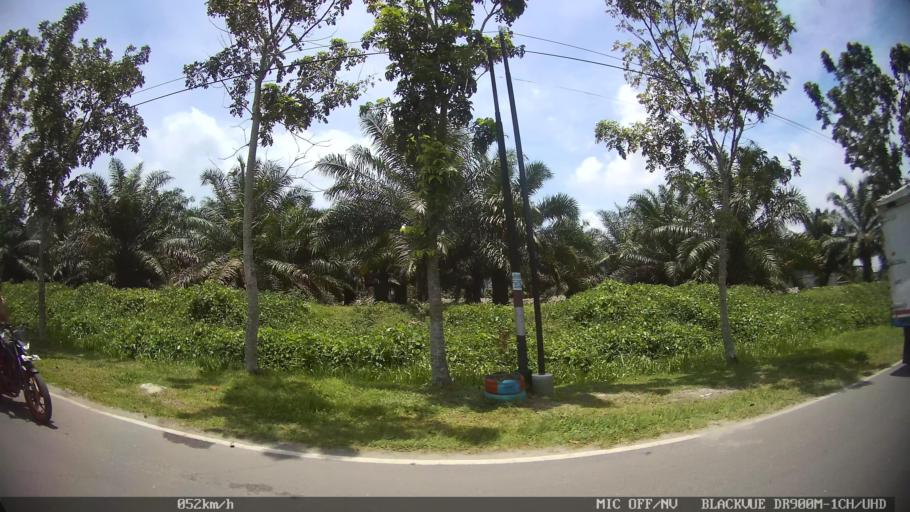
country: ID
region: North Sumatra
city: Percut
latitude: 3.5462
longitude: 98.8668
